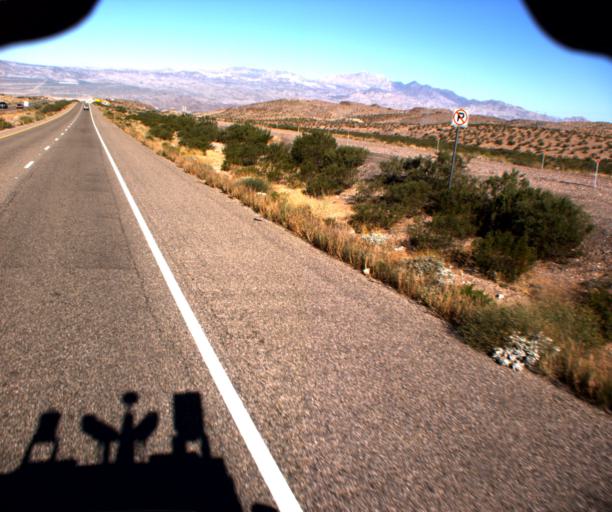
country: US
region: Nevada
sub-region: Clark County
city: Laughlin
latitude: 35.1855
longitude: -114.4790
